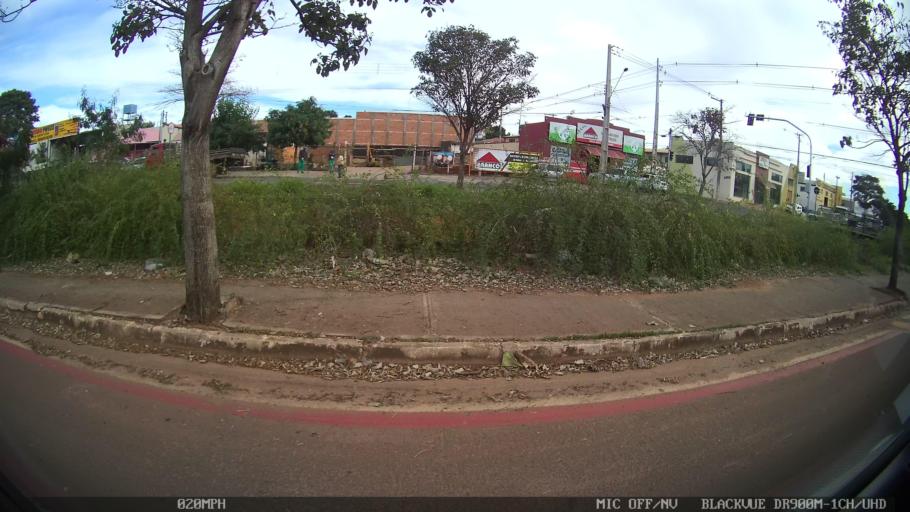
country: BR
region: Sao Paulo
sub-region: Catanduva
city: Catanduva
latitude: -21.1299
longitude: -48.9847
